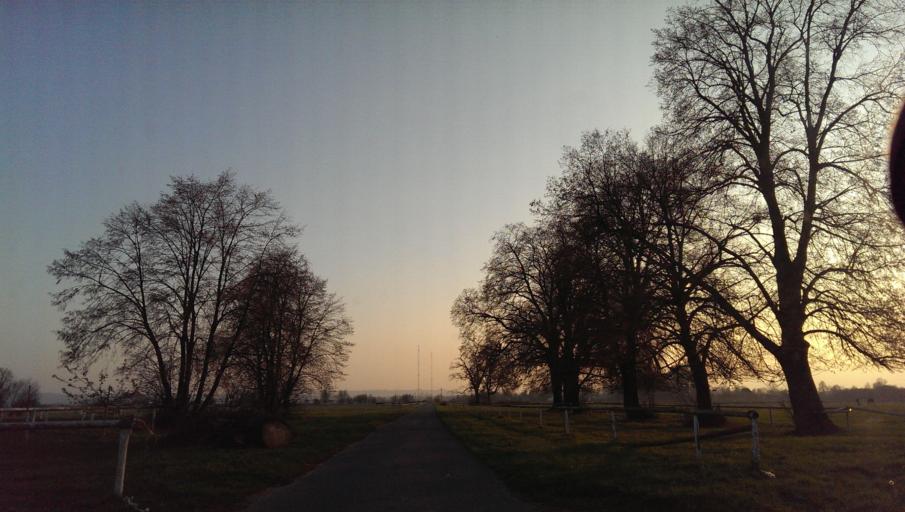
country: CZ
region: Zlin
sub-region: Okres Zlin
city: Napajedla
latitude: 49.1524
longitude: 17.5144
